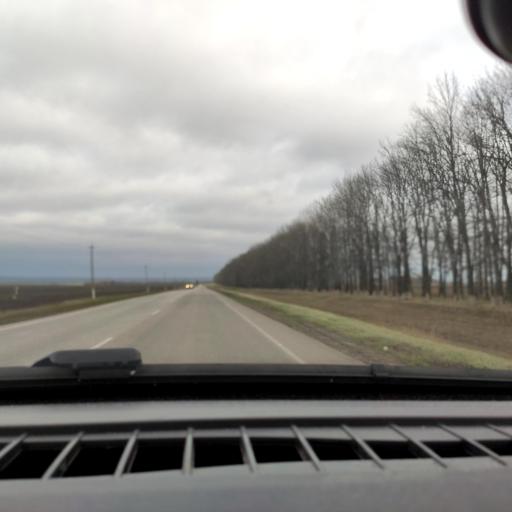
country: RU
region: Belgorod
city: Ilovka
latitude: 50.7442
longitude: 38.7107
